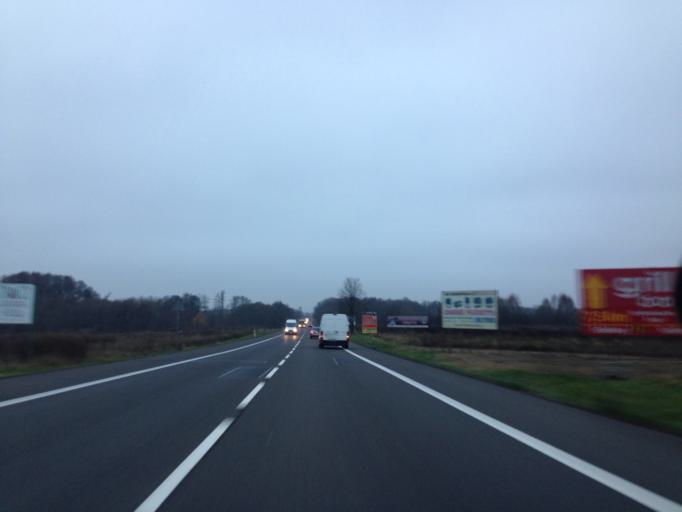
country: PL
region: Lodz Voivodeship
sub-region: Powiat zgierski
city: Strykow
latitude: 51.8735
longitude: 19.5751
